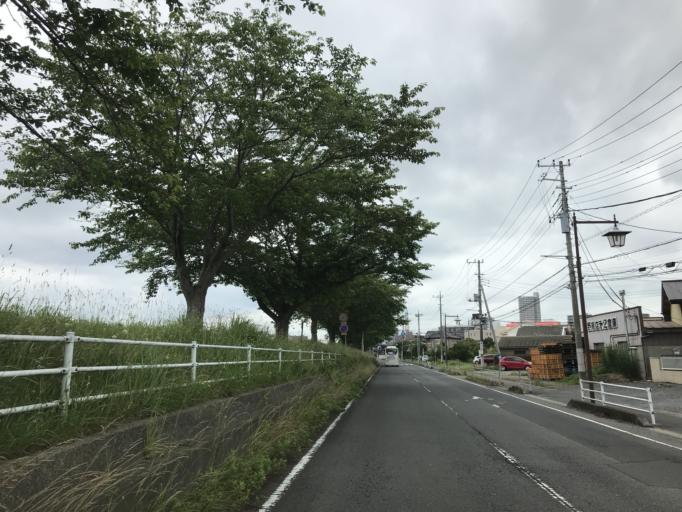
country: JP
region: Ibaraki
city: Ami
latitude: 36.0763
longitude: 140.2147
